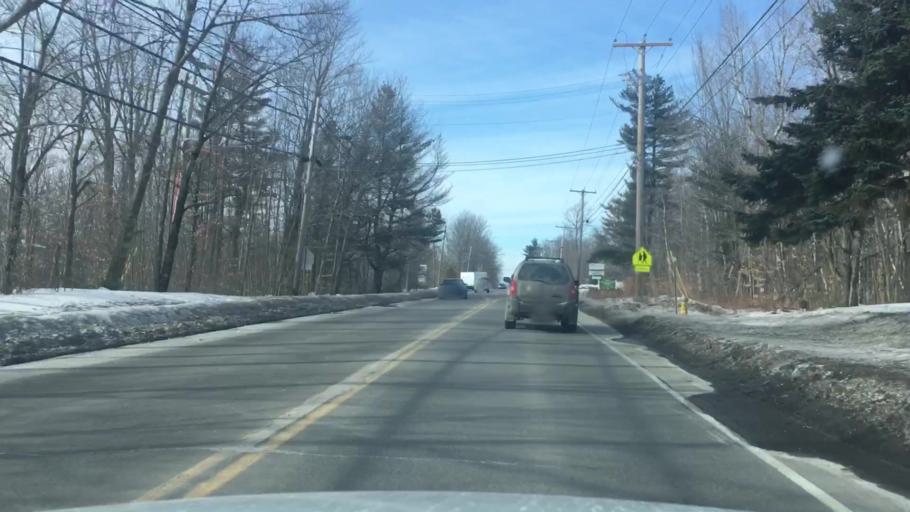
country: US
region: Maine
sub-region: Penobscot County
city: Bangor
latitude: 44.8300
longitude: -68.7855
